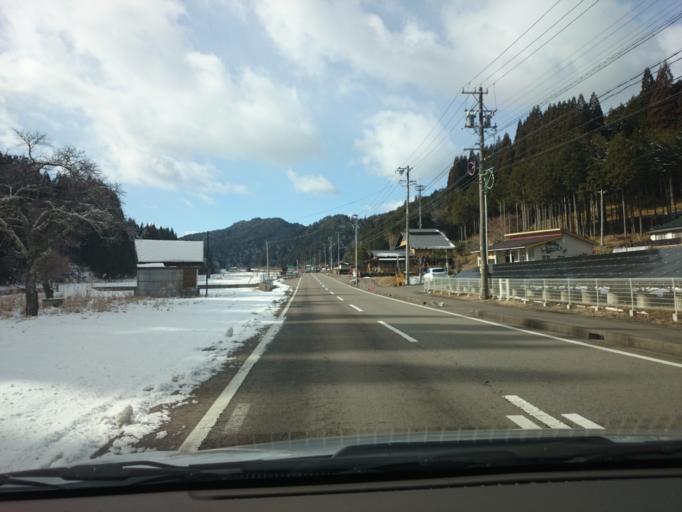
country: JP
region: Gifu
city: Gujo
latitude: 35.7529
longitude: 137.0420
